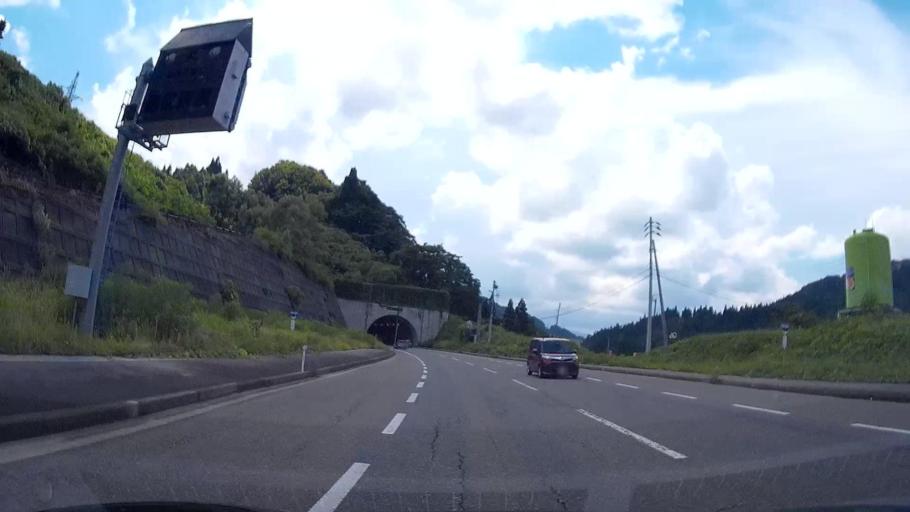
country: JP
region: Niigata
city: Tokamachi
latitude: 37.0092
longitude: 138.6441
